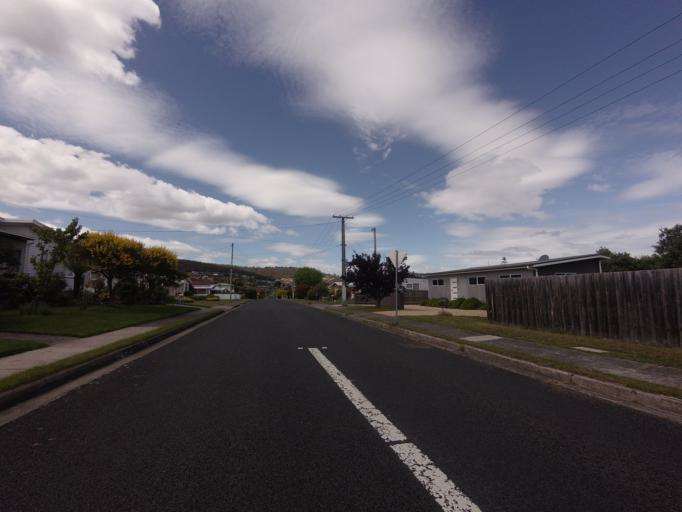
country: AU
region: Tasmania
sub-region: Clarence
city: Howrah
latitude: -42.8773
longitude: 147.3984
